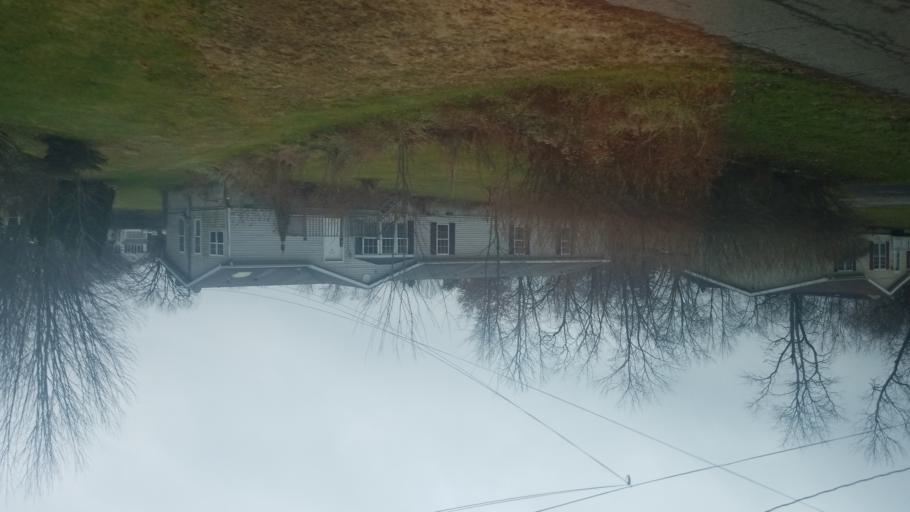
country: US
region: Ohio
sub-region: Crawford County
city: Galion
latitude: 40.7287
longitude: -82.7711
